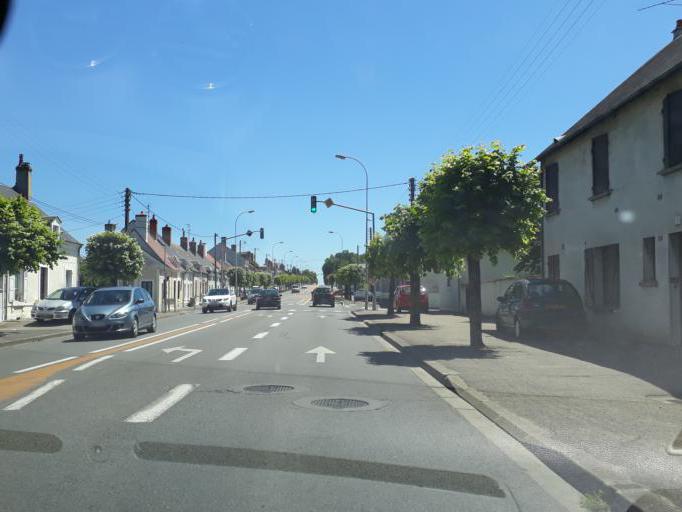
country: FR
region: Centre
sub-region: Departement du Cher
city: Mehun-sur-Yevre
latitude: 47.1446
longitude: 2.2232
